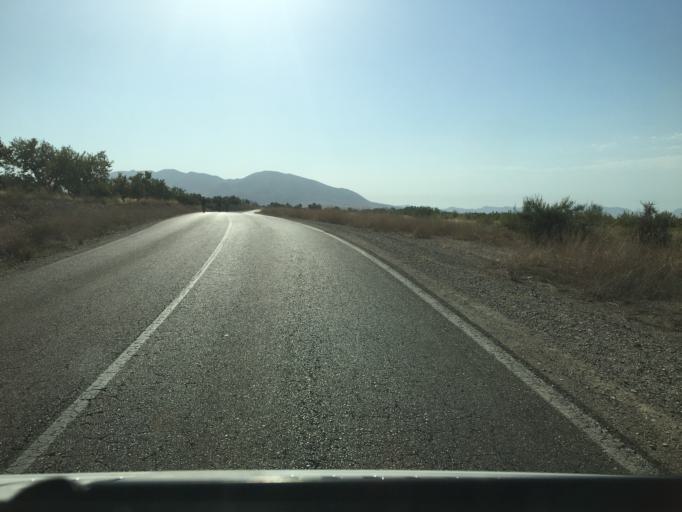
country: ES
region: Andalusia
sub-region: Provincia de Almeria
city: Huercal-Overa
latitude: 37.4699
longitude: -1.9076
